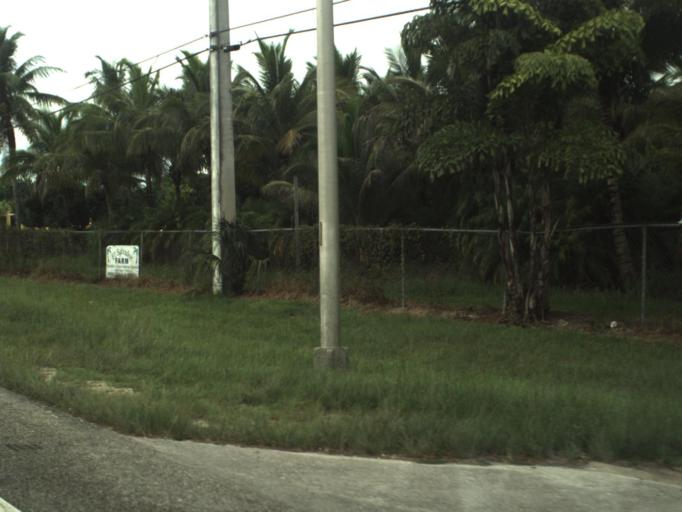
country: US
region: Florida
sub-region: Miami-Dade County
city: Richmond West
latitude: 25.6066
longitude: -80.4790
